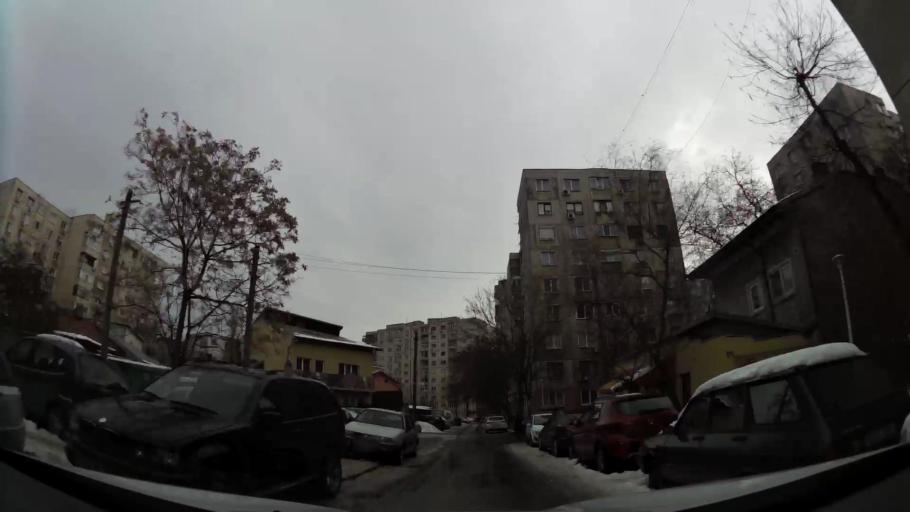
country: RO
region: Bucuresti
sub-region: Municipiul Bucuresti
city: Bucuresti
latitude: 44.4076
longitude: 26.0631
